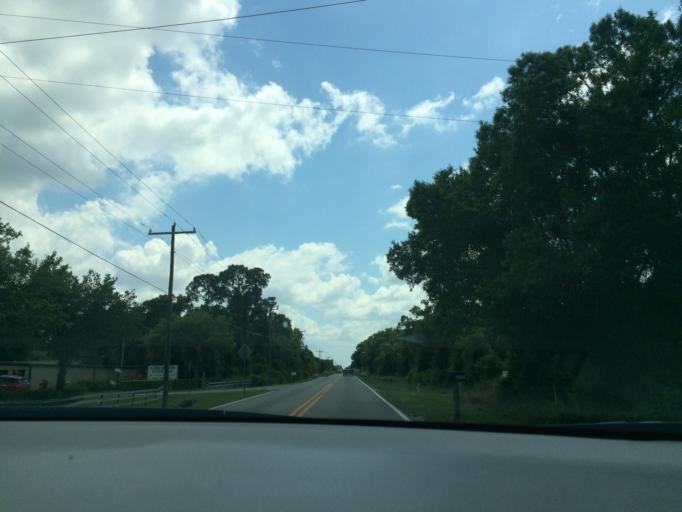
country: US
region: Florida
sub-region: Sarasota County
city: The Meadows
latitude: 27.4744
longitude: -82.3956
